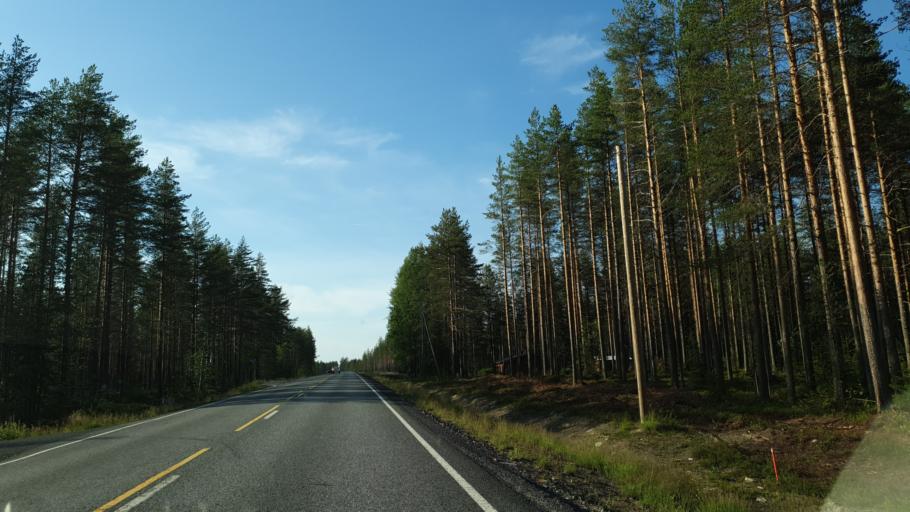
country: FI
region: Kainuu
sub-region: Kehys-Kainuu
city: Kuhmo
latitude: 64.0875
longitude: 29.4825
